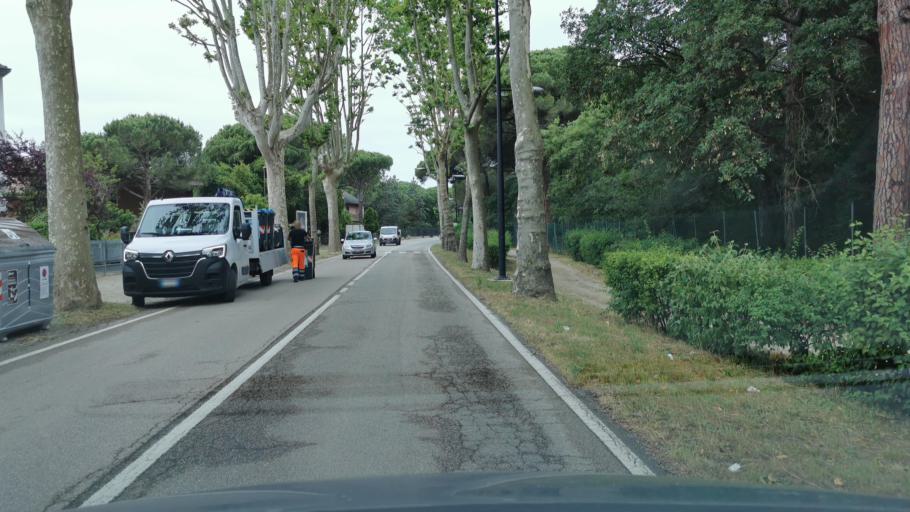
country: IT
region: Emilia-Romagna
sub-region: Provincia di Ravenna
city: Cervia
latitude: 44.2667
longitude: 12.3339
